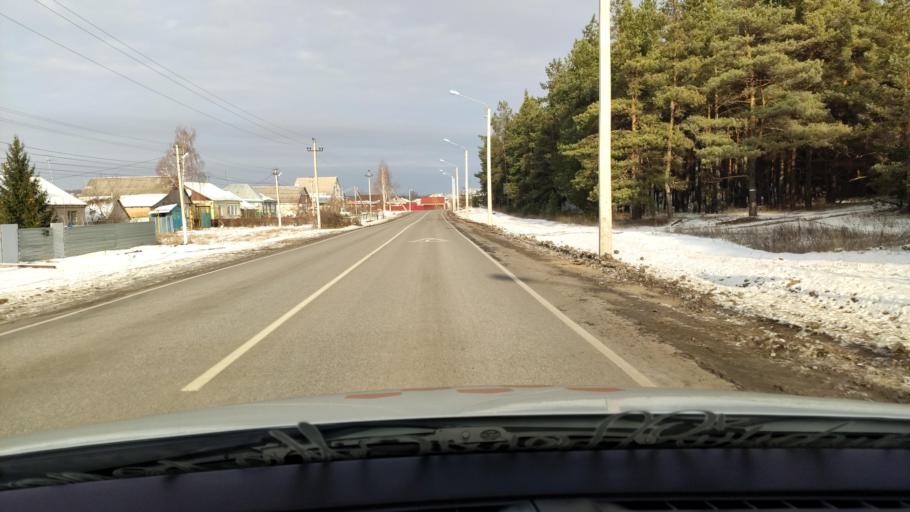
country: RU
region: Voronezj
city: Shilovo
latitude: 51.5952
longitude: 39.0308
